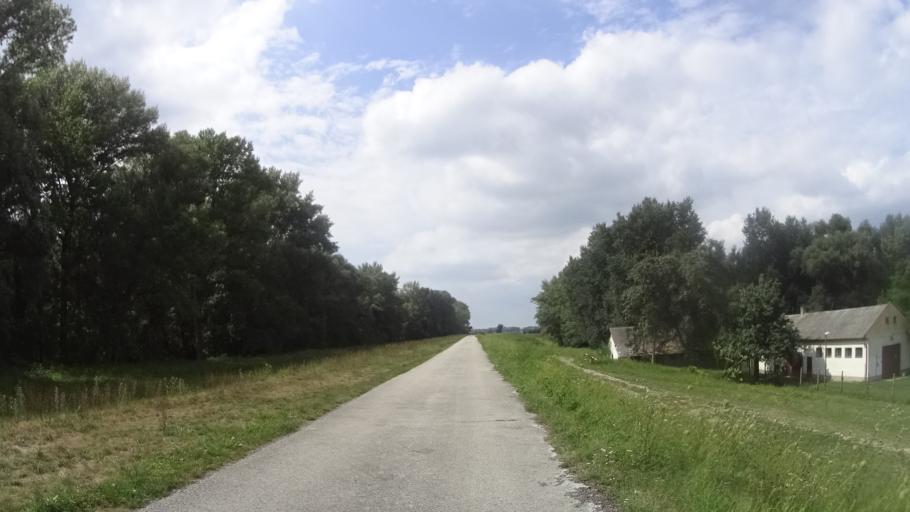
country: SK
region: Trnavsky
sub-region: Okres Dunajska Streda
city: Velky Meder
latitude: 47.7918
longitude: 17.6884
